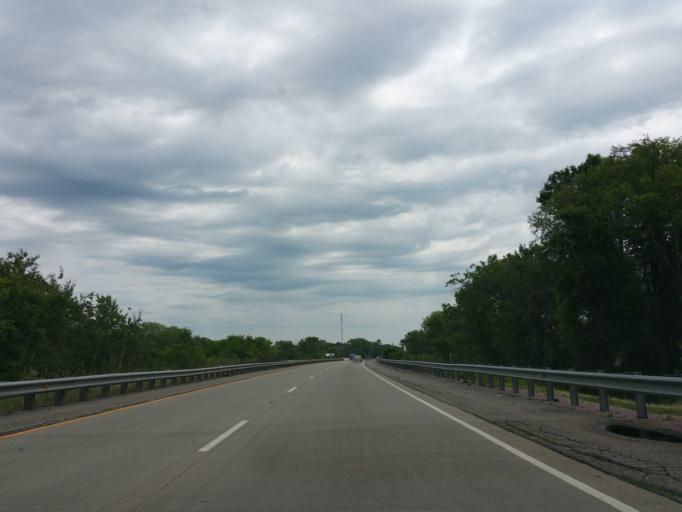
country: US
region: Wisconsin
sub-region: Juneau County
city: New Lisbon
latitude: 43.8929
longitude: -90.1684
